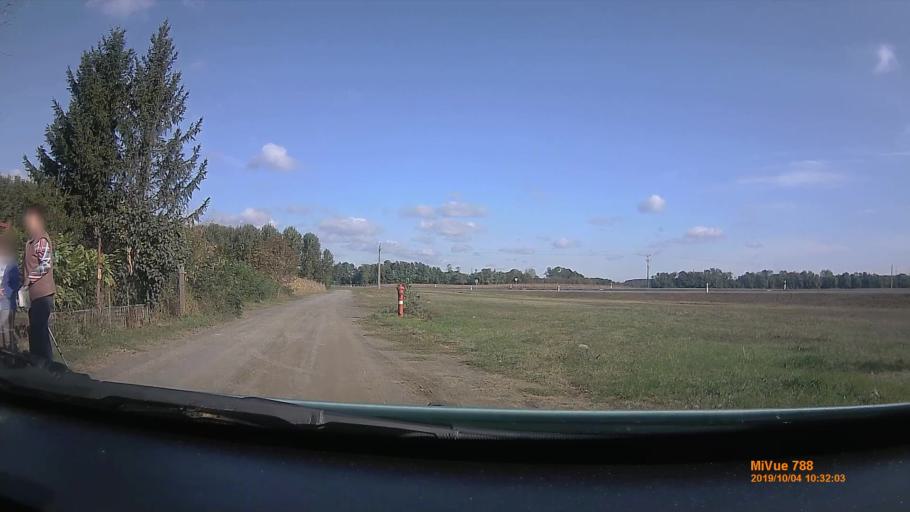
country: HU
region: Szabolcs-Szatmar-Bereg
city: Nyirtelek
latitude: 47.9636
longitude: 21.6574
